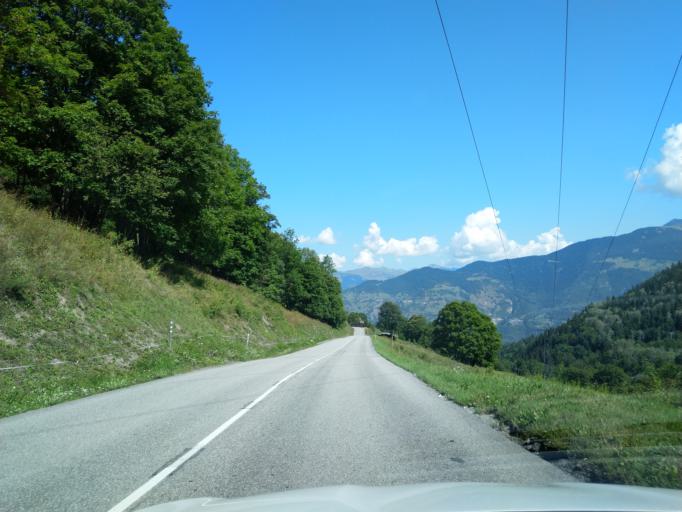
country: FR
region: Rhone-Alpes
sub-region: Departement de la Savoie
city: Meribel
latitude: 45.4140
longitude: 6.5550
